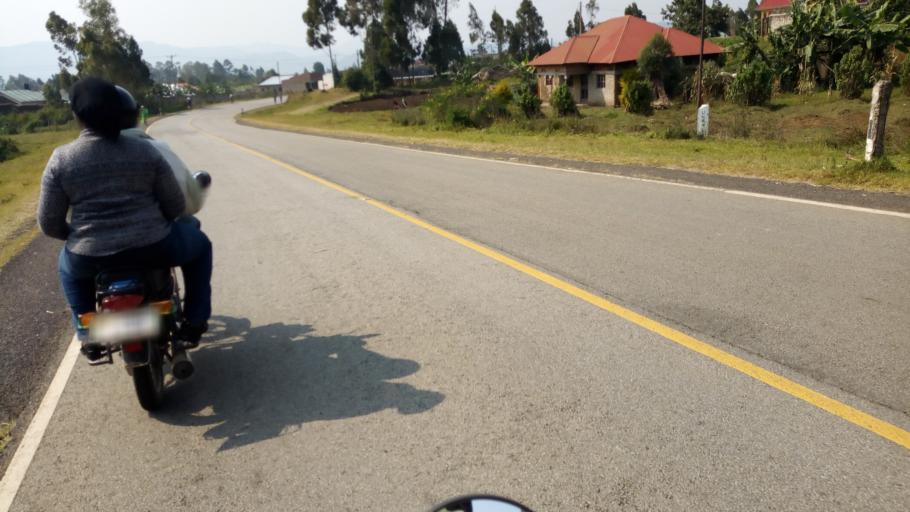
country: UG
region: Western Region
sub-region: Kisoro District
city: Kisoro
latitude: -1.3329
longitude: 29.7354
